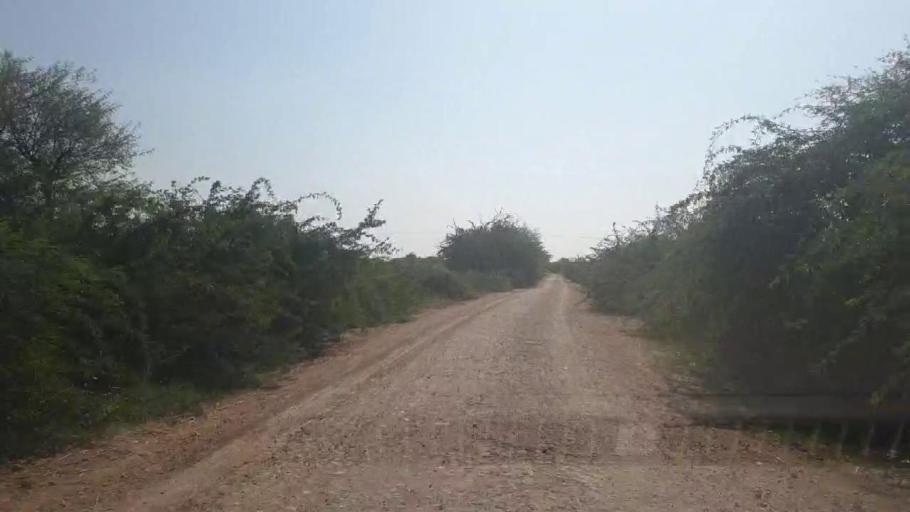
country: PK
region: Sindh
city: Badin
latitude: 24.5814
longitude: 68.8465
